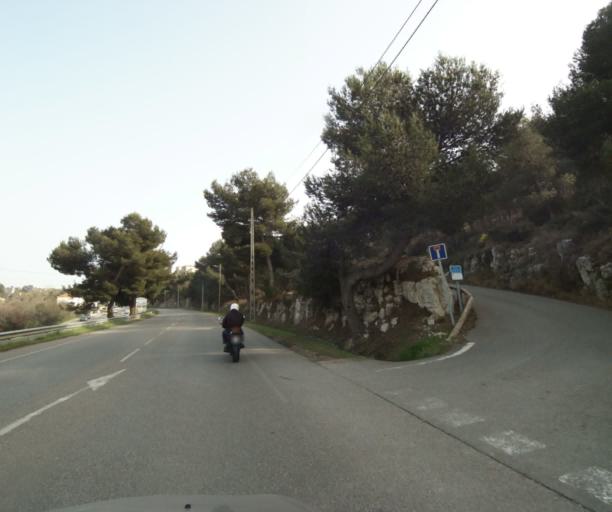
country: FR
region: Provence-Alpes-Cote d'Azur
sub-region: Departement des Bouches-du-Rhone
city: Les Pennes-Mirabeau
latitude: 43.4122
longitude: 5.3031
